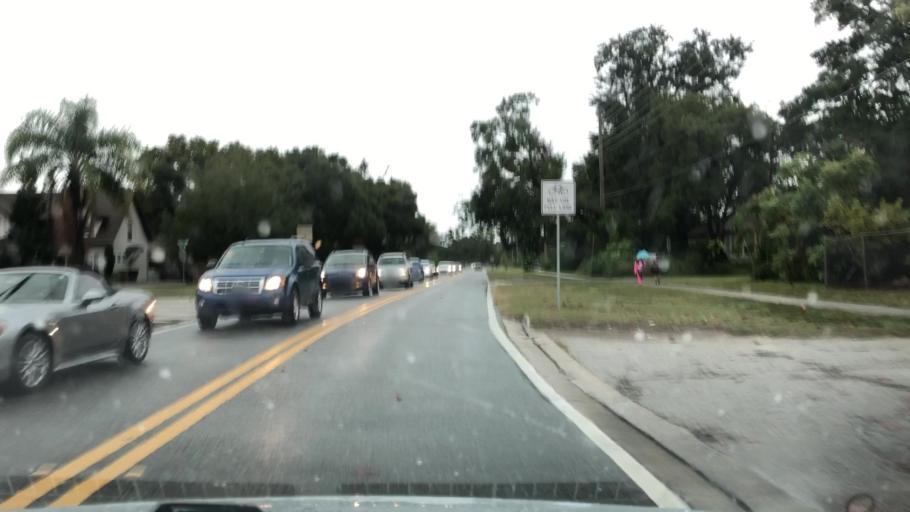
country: US
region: Florida
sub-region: Orange County
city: Conway
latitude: 28.5248
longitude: -81.3476
